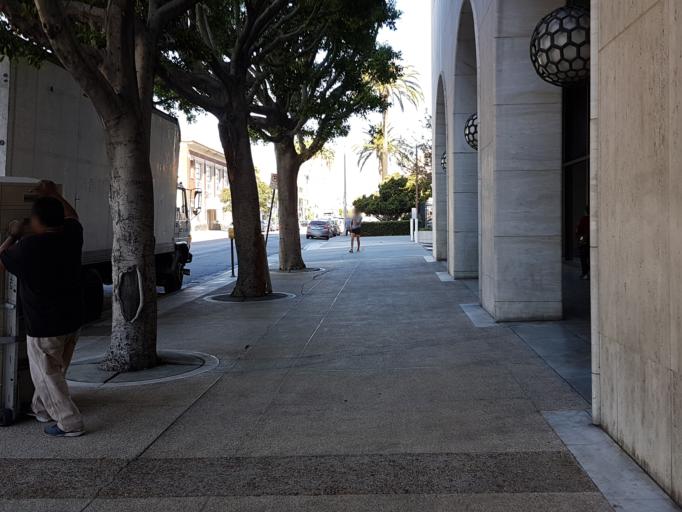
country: US
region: California
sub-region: Los Angeles County
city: Hollywood
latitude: 34.0624
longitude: -118.3078
